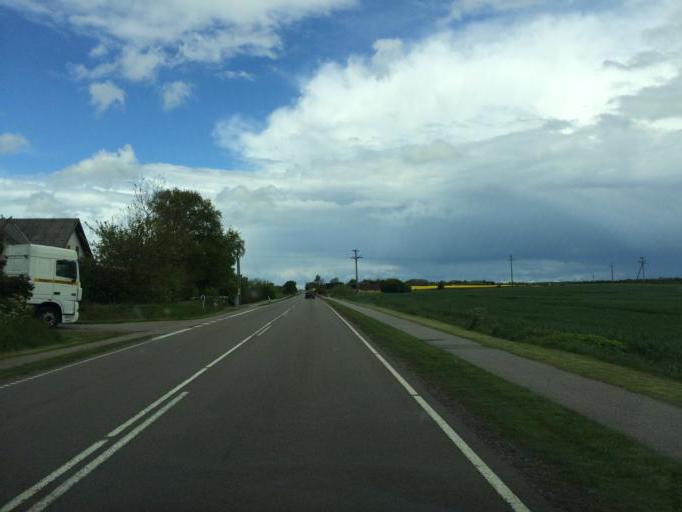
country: DK
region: North Denmark
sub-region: Vesthimmerland Kommune
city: Farso
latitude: 56.7439
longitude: 9.3147
